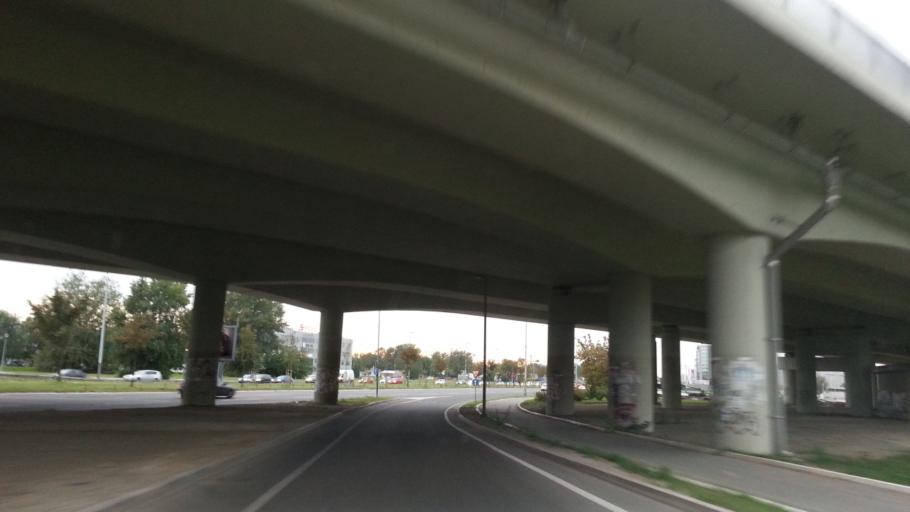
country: RS
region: Central Serbia
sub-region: Belgrade
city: Novi Beograd
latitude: 44.8041
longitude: 20.4222
